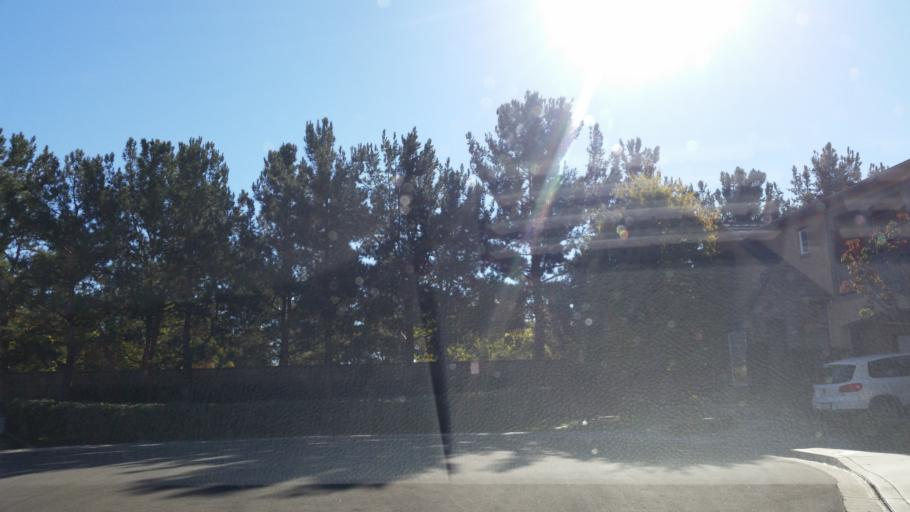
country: US
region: California
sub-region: Orange County
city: North Tustin
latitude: 33.7224
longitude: -117.7757
